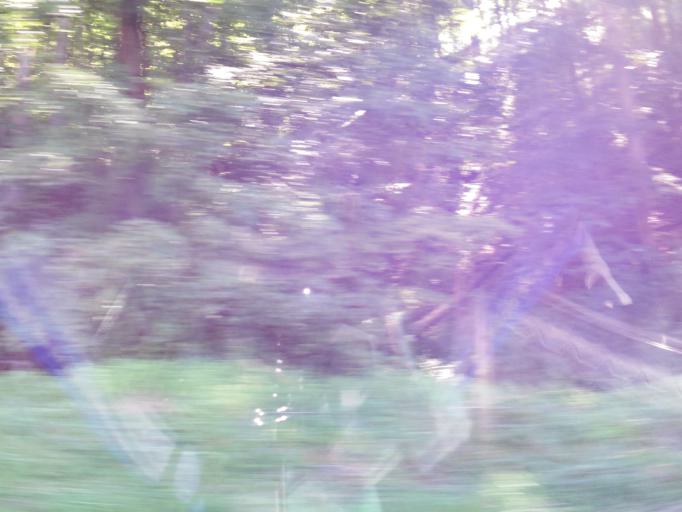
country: US
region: Kentucky
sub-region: Clay County
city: Manchester
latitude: 37.0997
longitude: -83.6663
